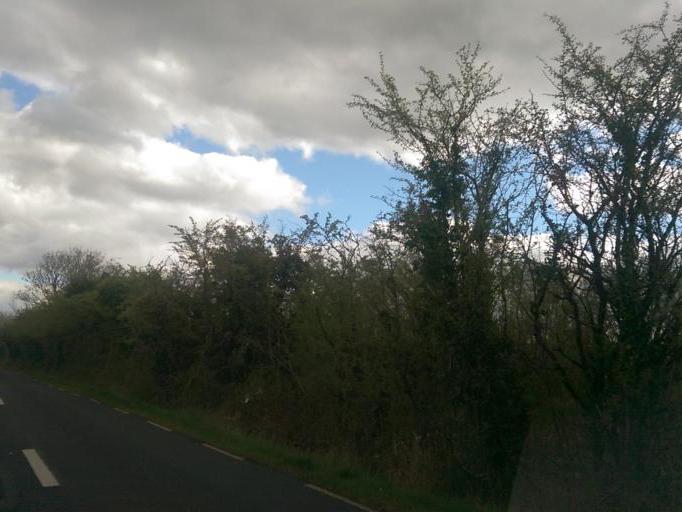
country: IE
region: Connaught
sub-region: County Galway
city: Ballinasloe
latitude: 53.3469
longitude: -8.2498
